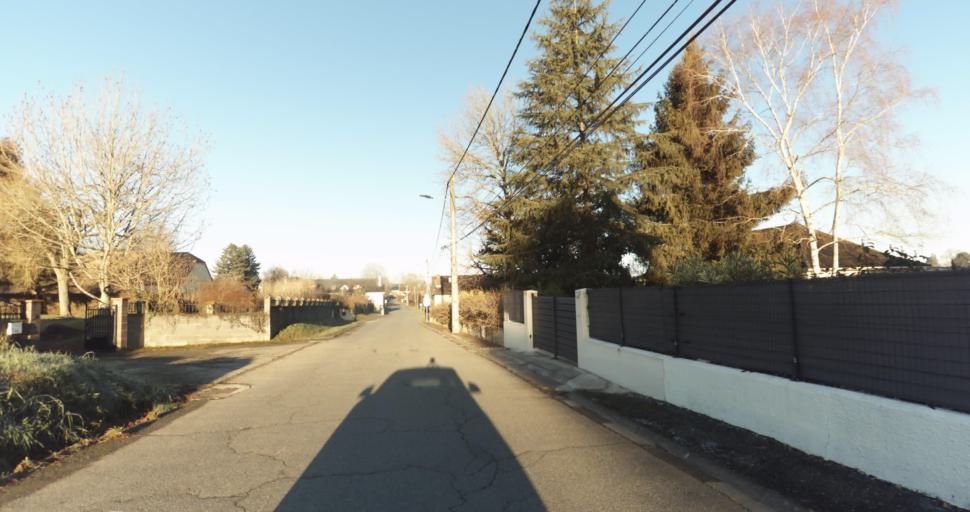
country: FR
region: Aquitaine
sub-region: Departement des Pyrenees-Atlantiques
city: Morlaas
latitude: 43.3345
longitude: -0.2718
